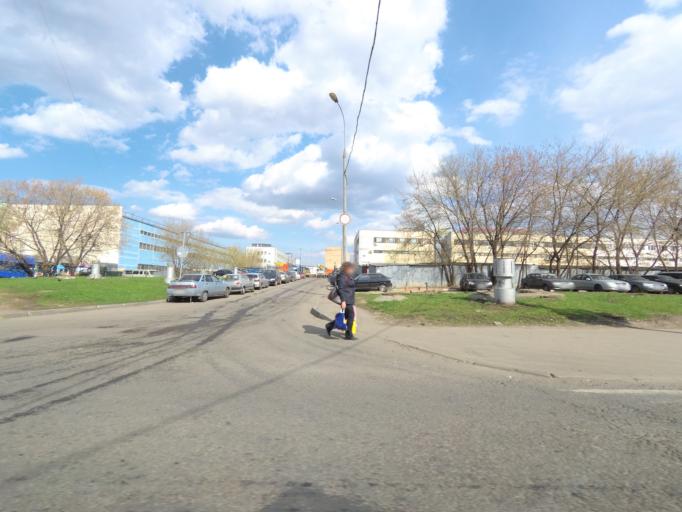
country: RU
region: Moscow
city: Gol'yanovo
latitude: 55.8041
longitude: 37.8300
